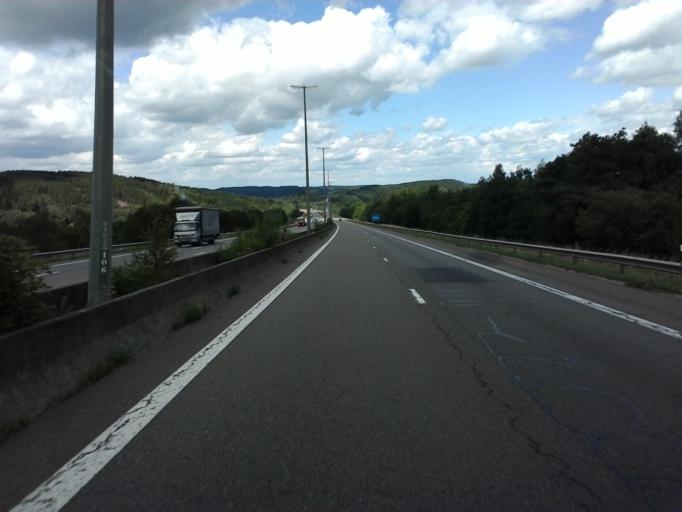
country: BE
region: Wallonia
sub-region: Province du Luxembourg
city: Manhay
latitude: 50.2874
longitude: 5.7275
